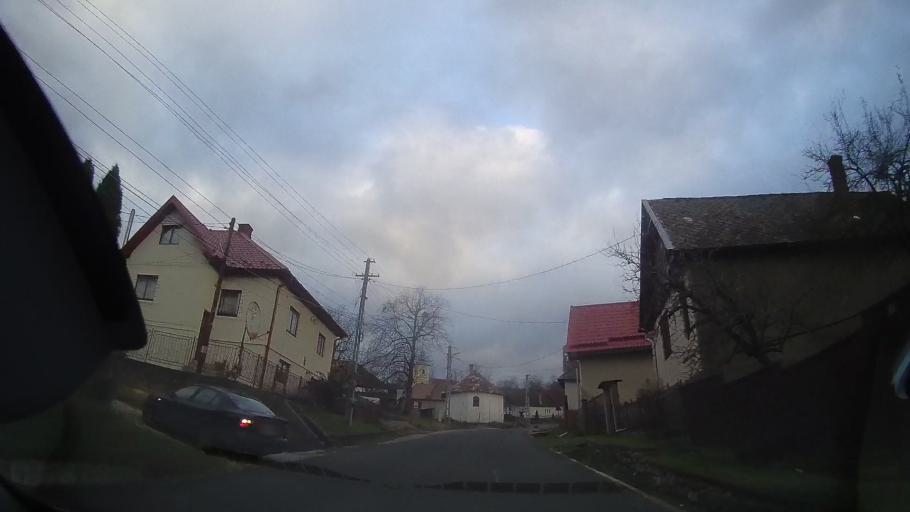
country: RO
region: Cluj
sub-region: Comuna Calatele
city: Calatele
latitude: 46.7811
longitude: 23.0314
